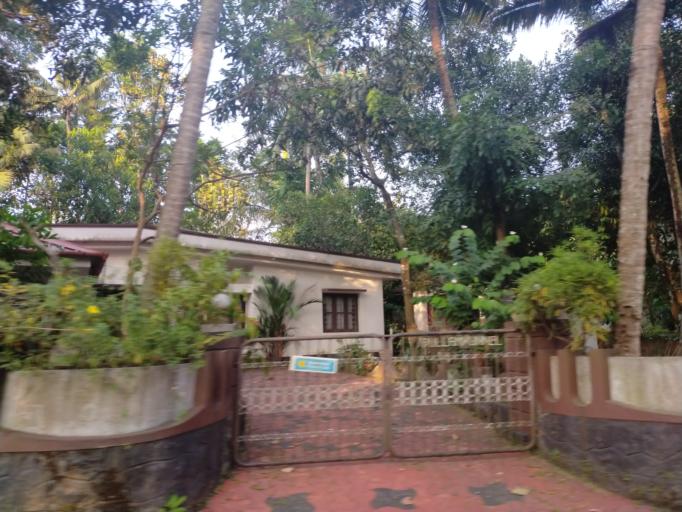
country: IN
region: Kerala
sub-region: Kottayam
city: Vaikam
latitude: 9.7469
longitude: 76.5122
